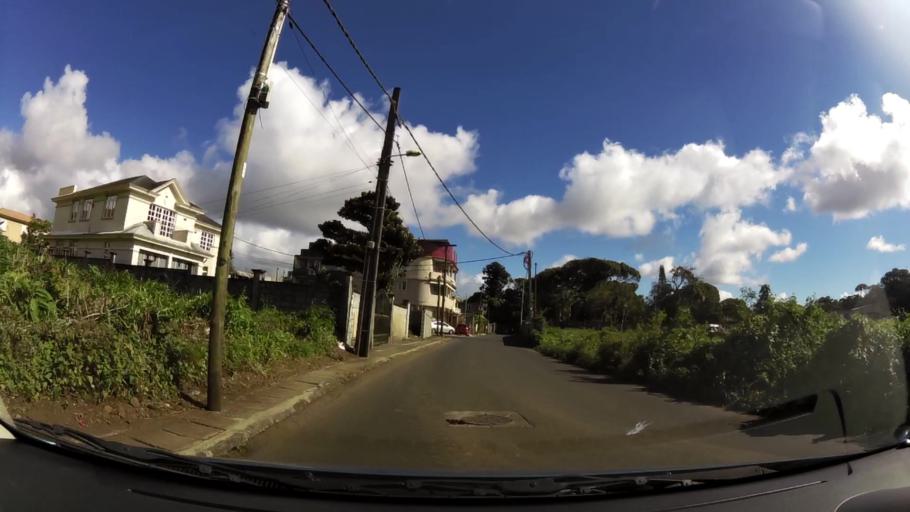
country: MU
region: Plaines Wilhems
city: Curepipe
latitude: -20.3240
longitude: 57.5226
